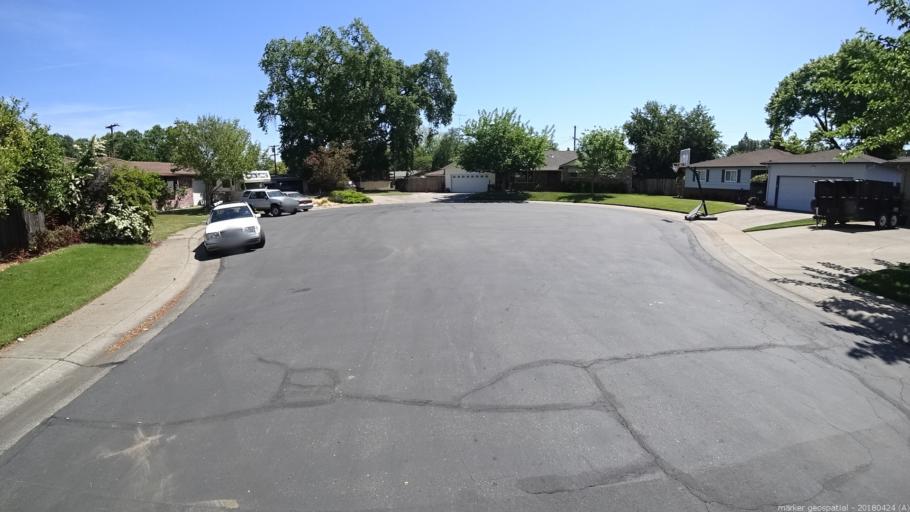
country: US
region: California
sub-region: Yolo County
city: West Sacramento
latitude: 38.5657
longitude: -121.5366
